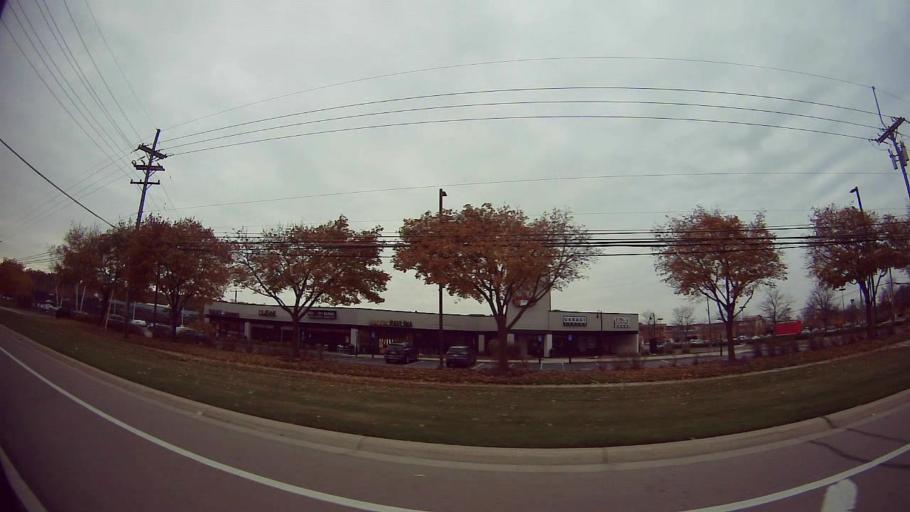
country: US
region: Michigan
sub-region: Oakland County
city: Franklin
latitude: 42.5246
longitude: -83.3503
